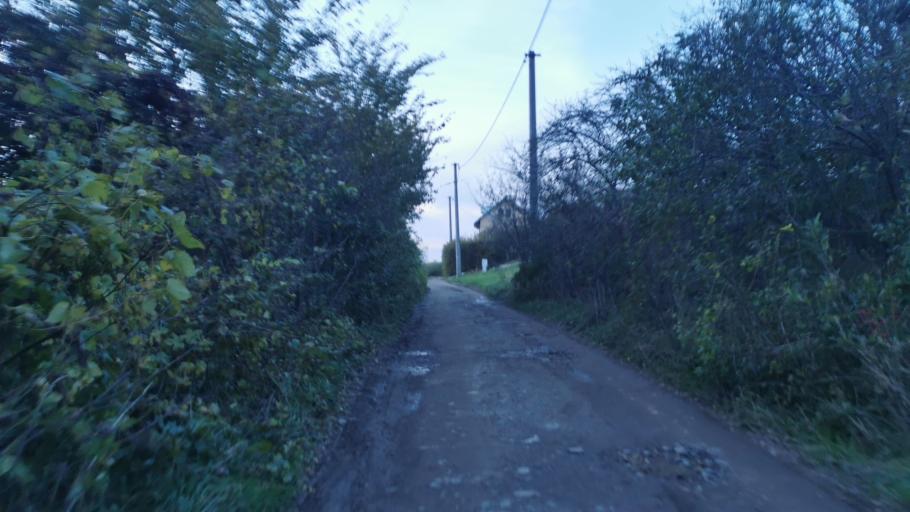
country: SK
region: Trnavsky
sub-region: Okres Skalica
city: Skalica
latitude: 48.8191
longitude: 17.2378
